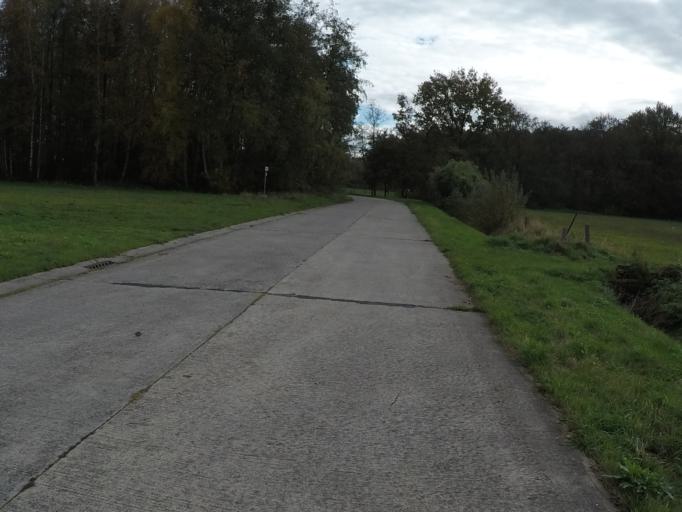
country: BE
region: Flanders
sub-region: Provincie Antwerpen
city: Nijlen
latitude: 51.1579
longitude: 4.6498
